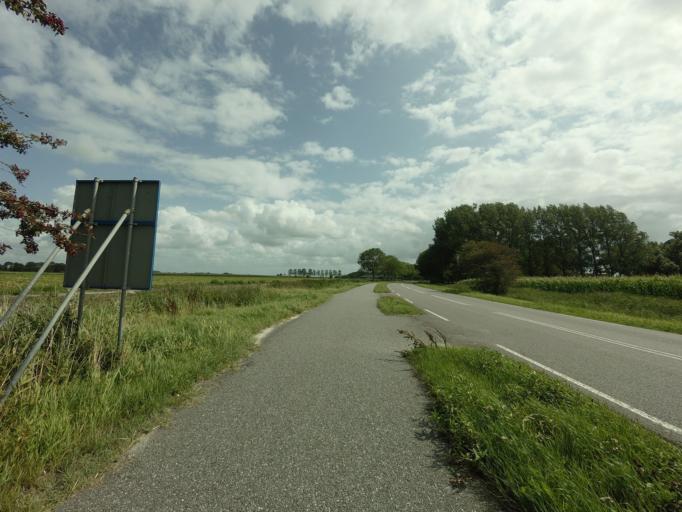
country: NL
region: Friesland
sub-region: Gemeente Harlingen
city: Harlingen
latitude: 53.1360
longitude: 5.4635
